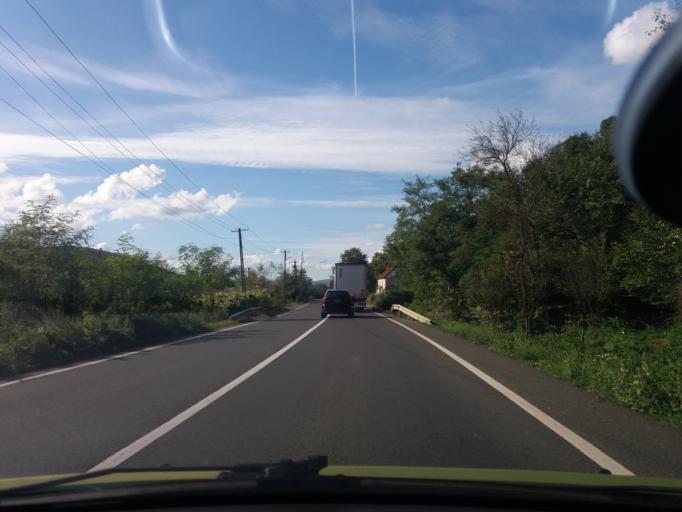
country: RO
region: Arad
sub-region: Comuna Bata
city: Bata
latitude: 46.0528
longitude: 22.0505
